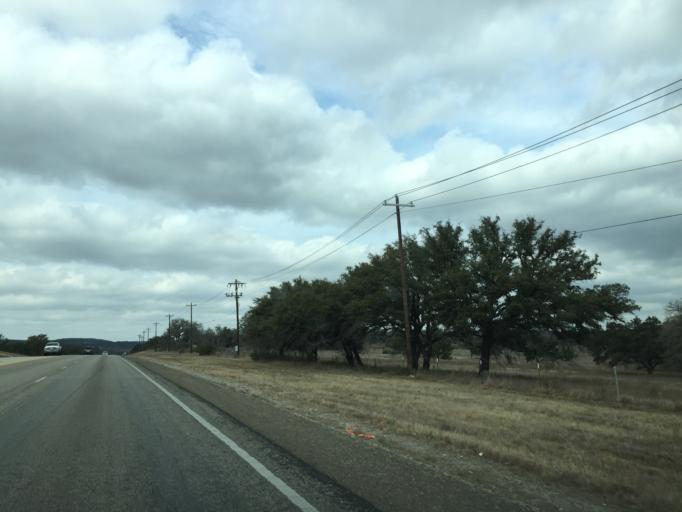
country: US
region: Texas
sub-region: Travis County
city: Briarcliff
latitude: 30.4150
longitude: -98.1180
